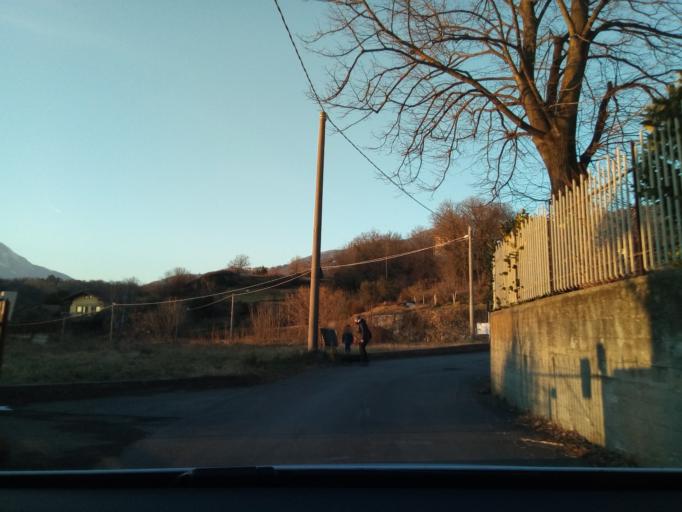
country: IT
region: Piedmont
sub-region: Provincia di Torino
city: Chiaverano
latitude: 45.4960
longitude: 7.9077
